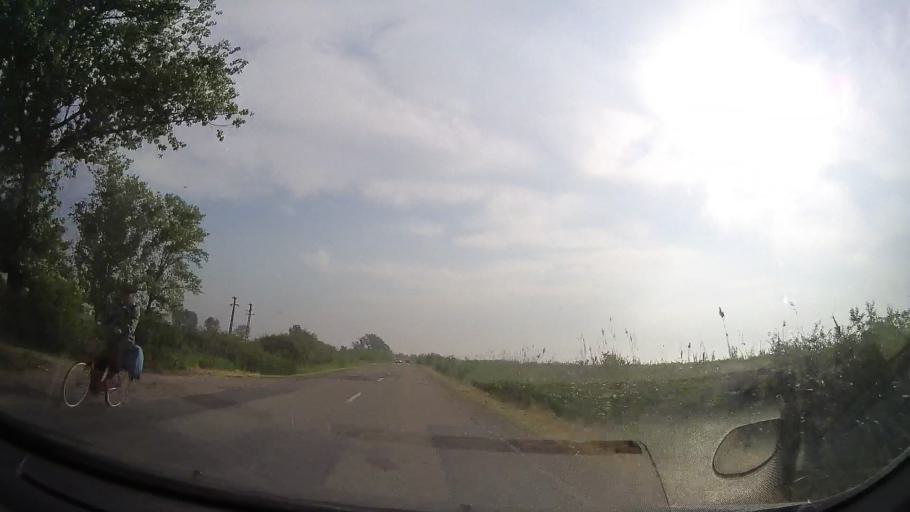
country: RO
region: Timis
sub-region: Comuna Peciu Nou
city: Peciu Nou
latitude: 45.5923
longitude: 21.0406
